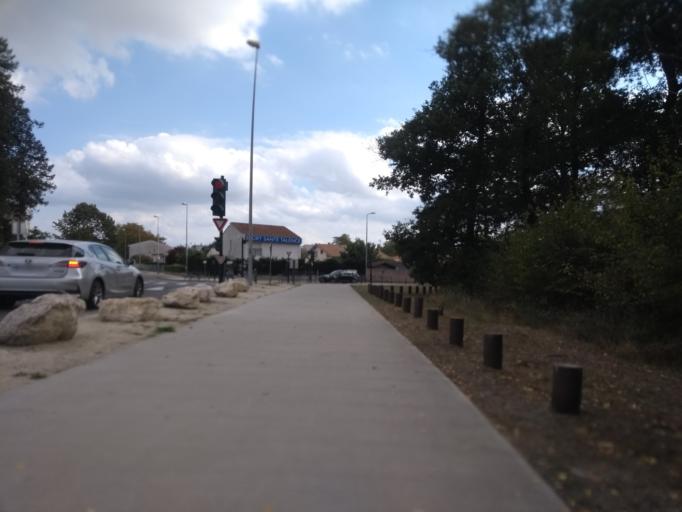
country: FR
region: Aquitaine
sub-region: Departement de la Gironde
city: Talence
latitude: 44.7937
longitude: -0.5924
